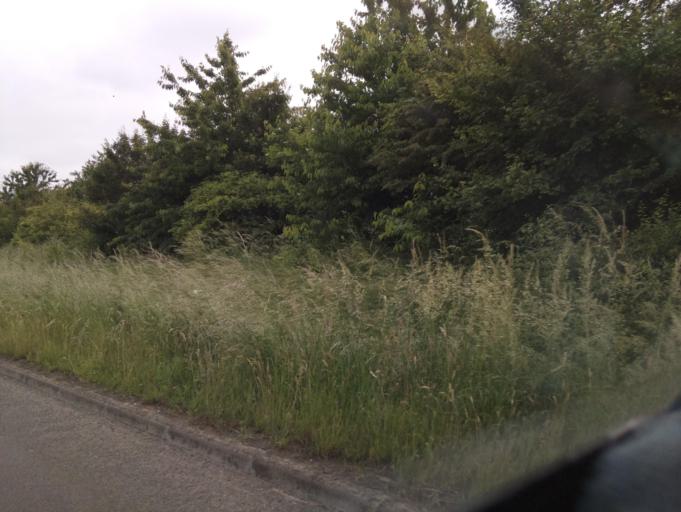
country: GB
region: England
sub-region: District of Rutland
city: Oakham
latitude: 52.6625
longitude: -0.7167
